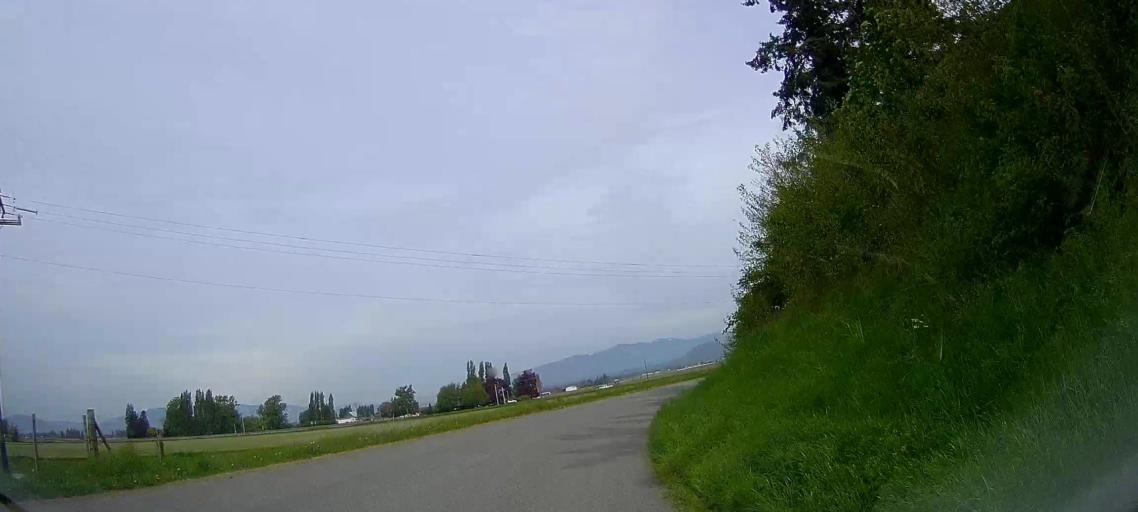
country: US
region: Washington
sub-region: Skagit County
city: Mount Vernon
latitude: 48.3953
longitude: -122.4478
